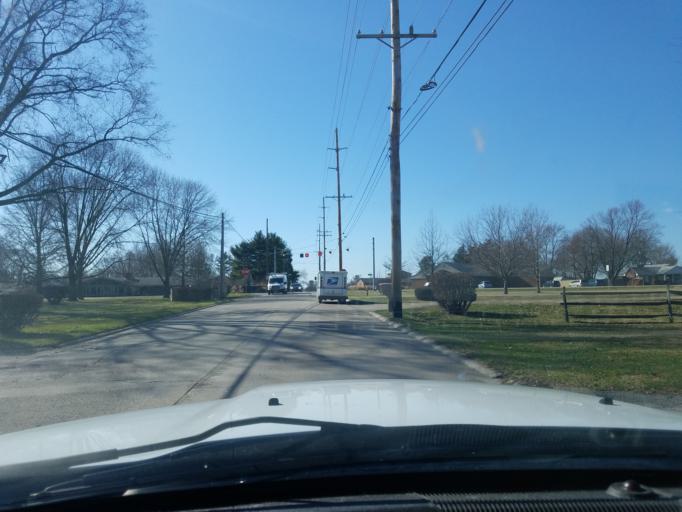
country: US
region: Indiana
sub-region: Shelby County
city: Shelbyville
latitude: 39.5047
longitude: -85.7706
